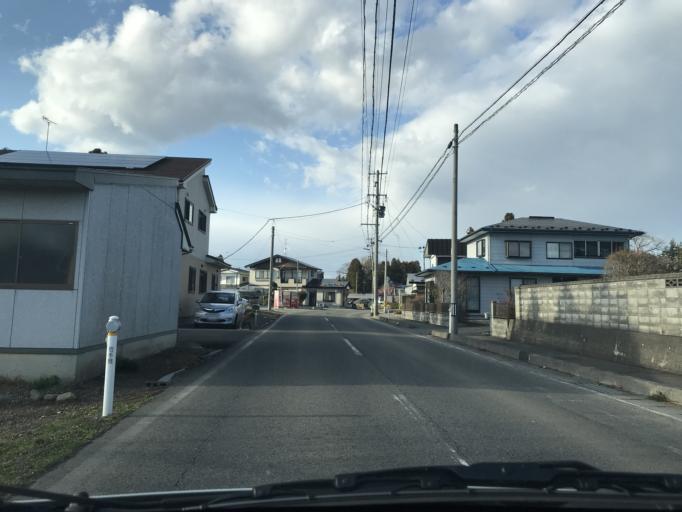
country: JP
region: Iwate
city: Kitakami
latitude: 39.3152
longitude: 141.0681
